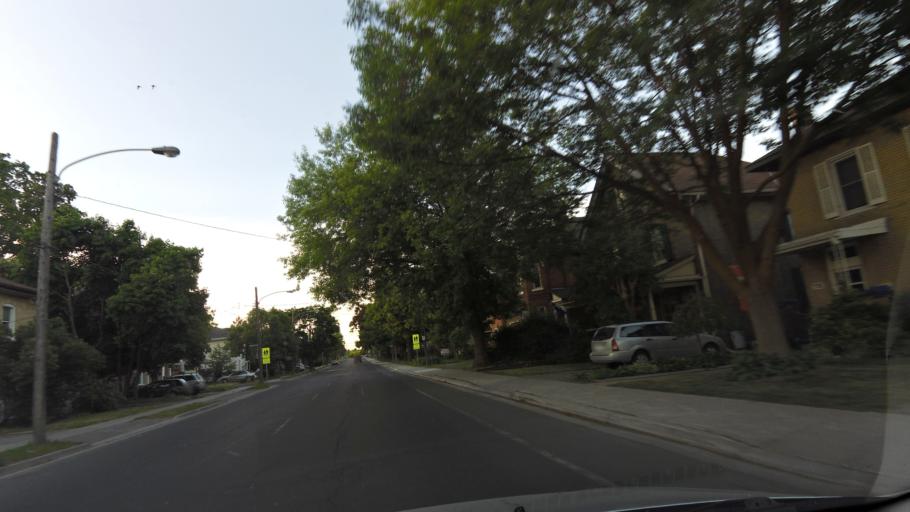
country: CA
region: Ontario
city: Peterborough
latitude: 44.3178
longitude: -78.3185
